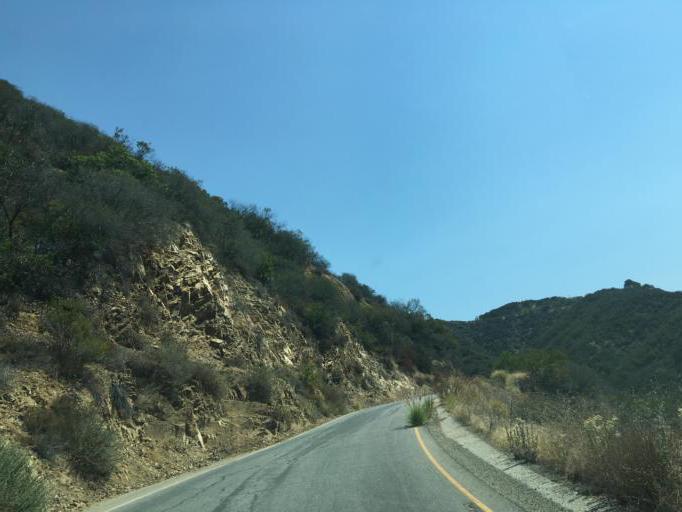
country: US
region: California
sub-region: Los Angeles County
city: Topanga
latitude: 34.0568
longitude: -118.6022
